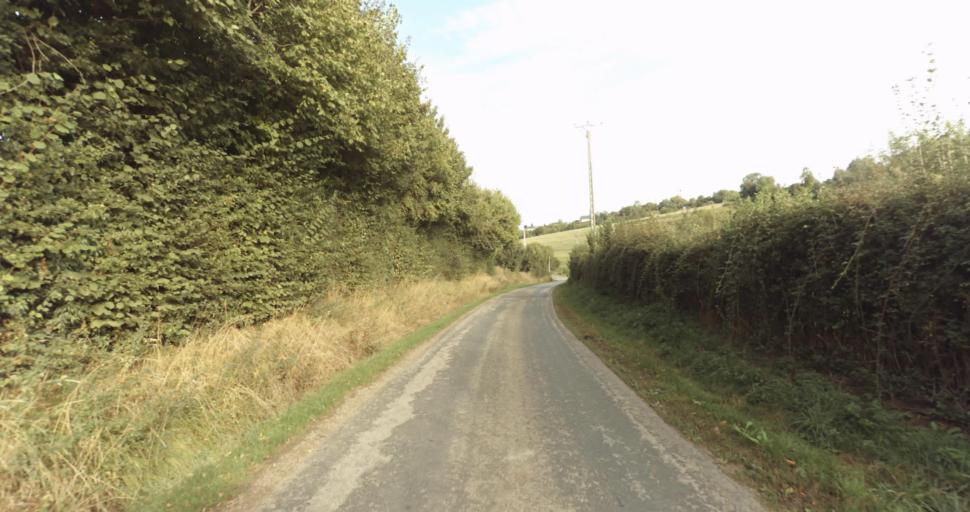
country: FR
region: Lower Normandy
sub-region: Departement de l'Orne
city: Vimoutiers
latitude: 48.8728
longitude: 0.2393
